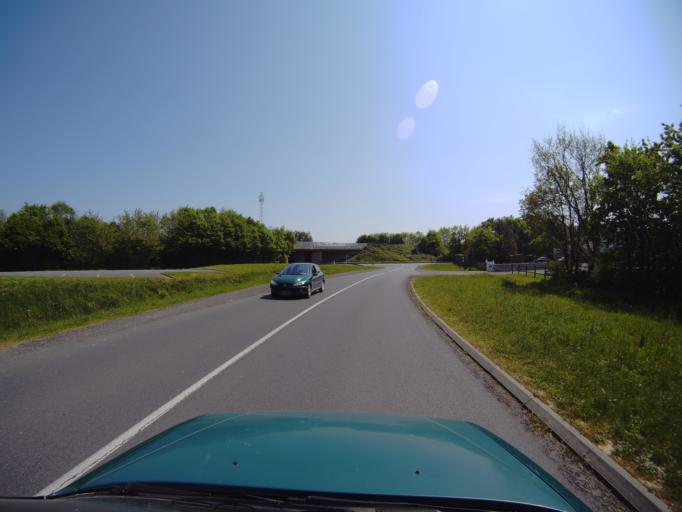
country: FR
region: Pays de la Loire
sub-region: Departement de la Vendee
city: Bouffere
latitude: 46.9520
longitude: -1.3487
